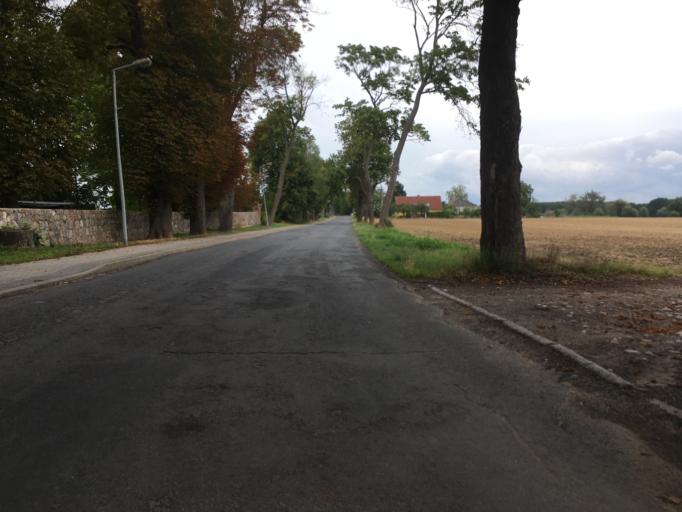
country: DE
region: Brandenburg
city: Prenzlau
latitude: 53.2293
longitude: 13.8430
